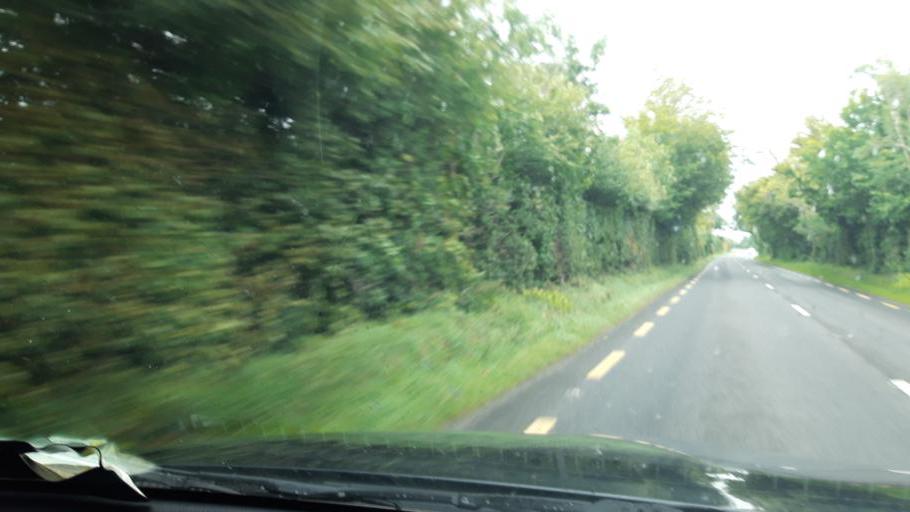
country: IE
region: Leinster
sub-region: Loch Garman
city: New Ross
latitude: 52.4292
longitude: -6.8189
